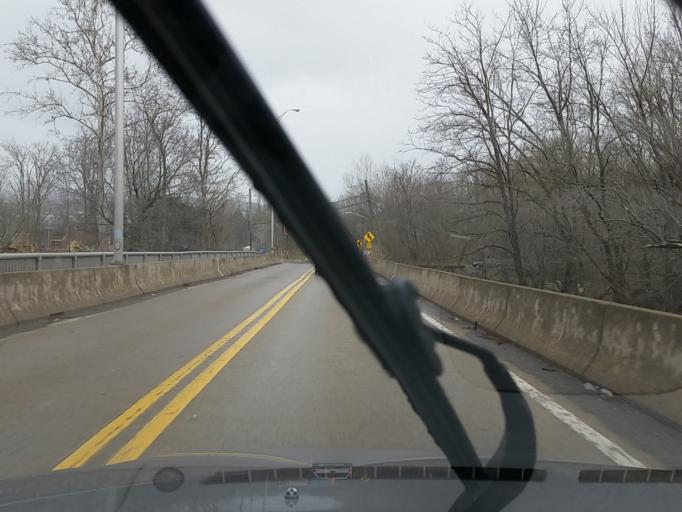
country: US
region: Pennsylvania
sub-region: Luzerne County
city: Nanticoke
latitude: 41.2115
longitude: -76.0039
